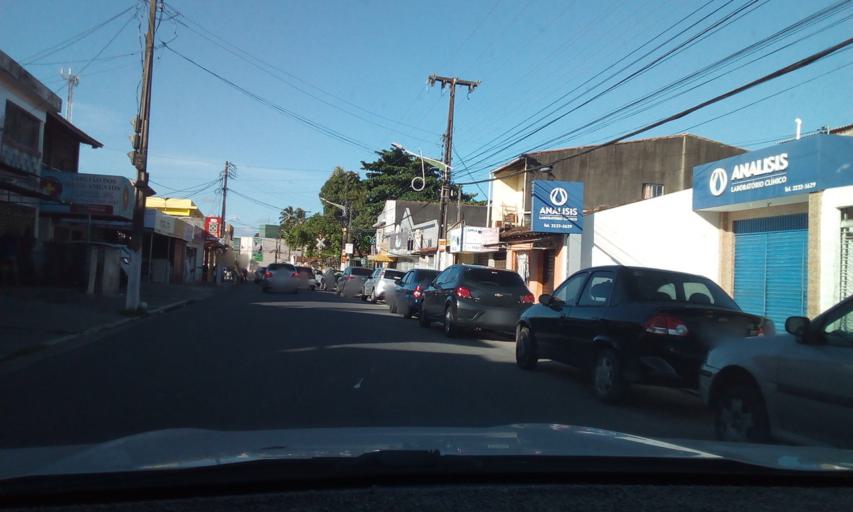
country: BR
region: Paraiba
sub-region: Bayeux
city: Bayeux
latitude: -7.1276
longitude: -34.9296
